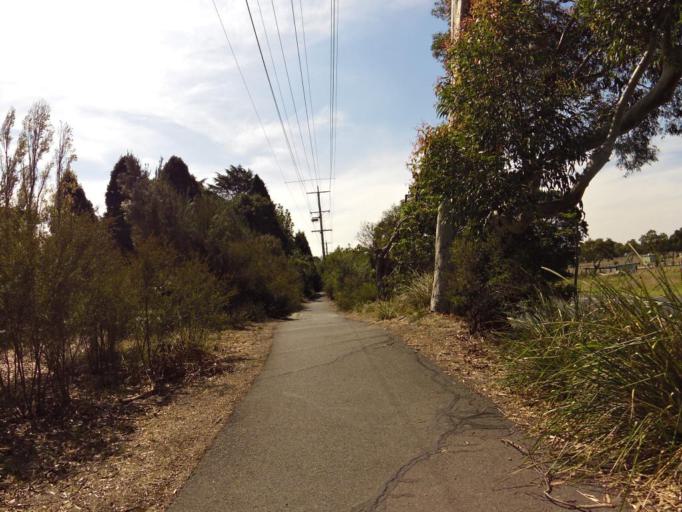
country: AU
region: Victoria
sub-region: Mornington Peninsula
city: Tyabb
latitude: -38.2452
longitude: 145.1914
